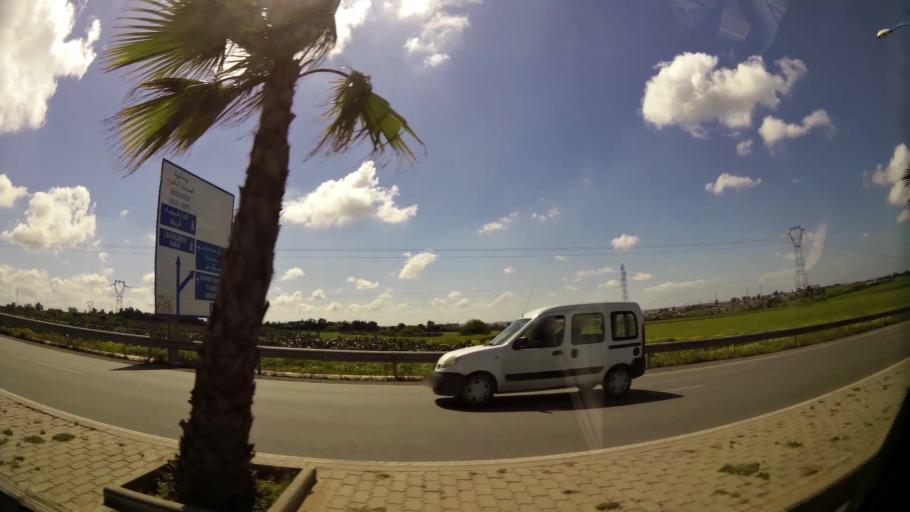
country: MA
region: Grand Casablanca
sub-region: Casablanca
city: Casablanca
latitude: 33.5142
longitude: -7.6137
